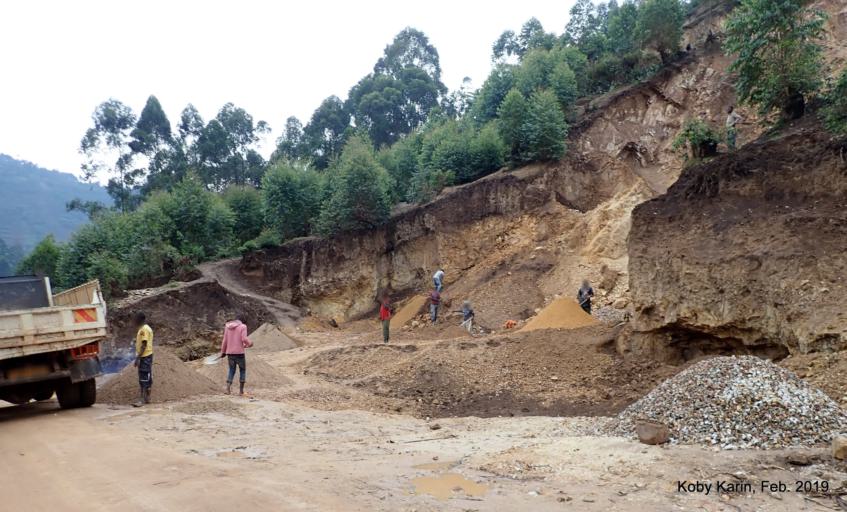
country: UG
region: Western Region
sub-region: Kabale District
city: Kabale
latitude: -1.2512
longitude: 29.9677
